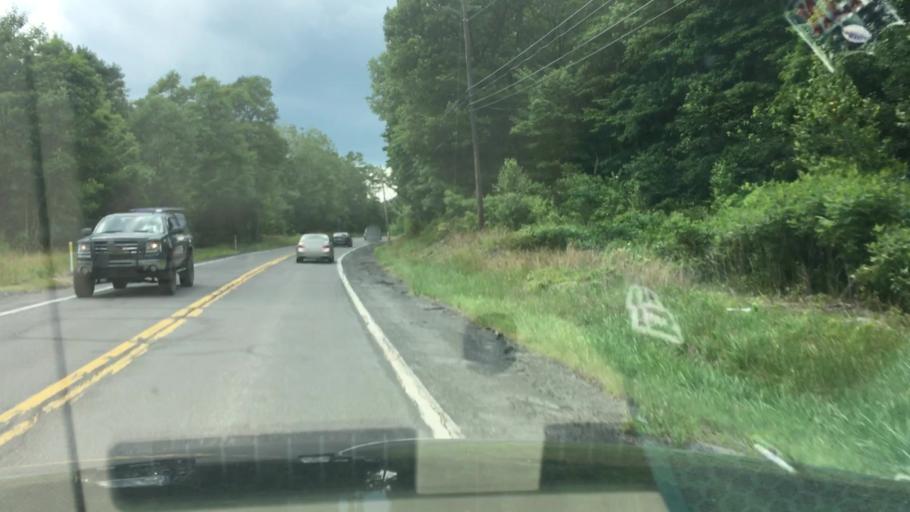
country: US
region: Pennsylvania
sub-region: Schuylkill County
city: Minersville
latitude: 40.7003
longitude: -76.3137
